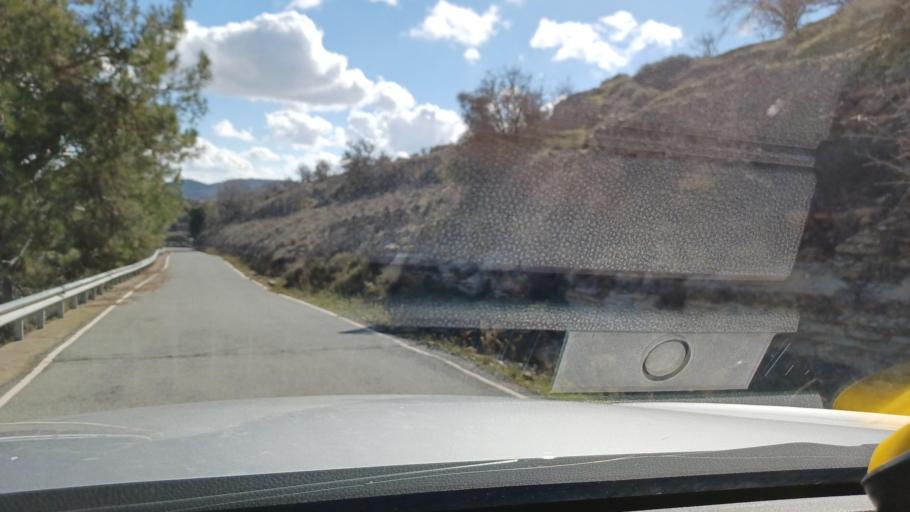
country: CY
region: Limassol
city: Pachna
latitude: 34.8243
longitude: 32.7807
